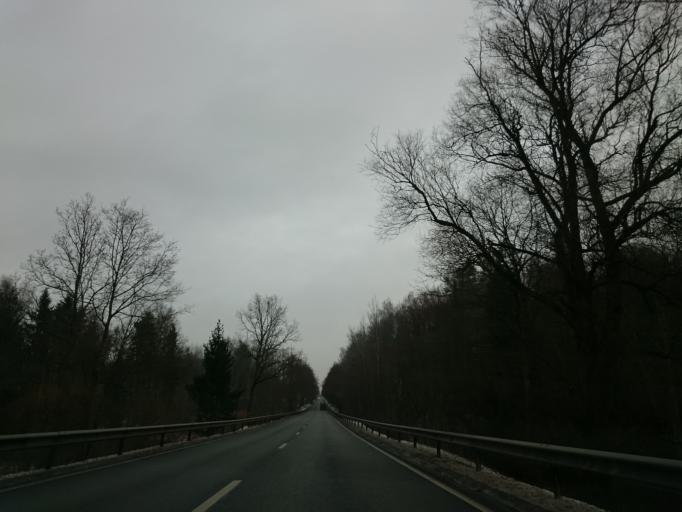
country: LV
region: Seja
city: Loja
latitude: 57.1502
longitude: 24.6821
